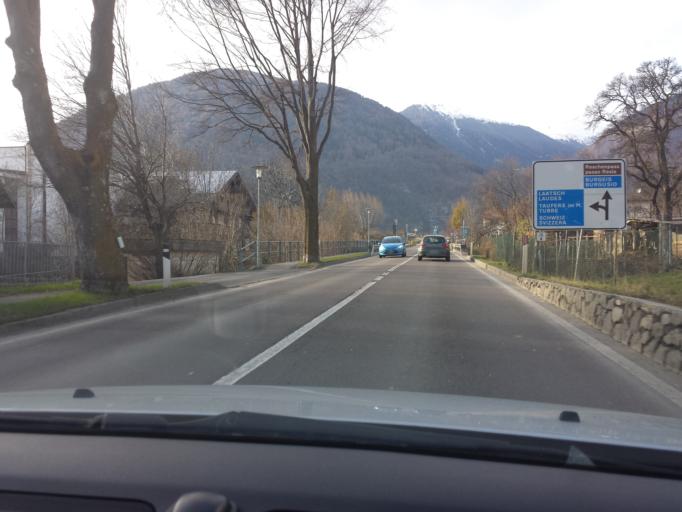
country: IT
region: Trentino-Alto Adige
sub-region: Bolzano
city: Malles Venosta
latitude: 46.6872
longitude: 10.5438
